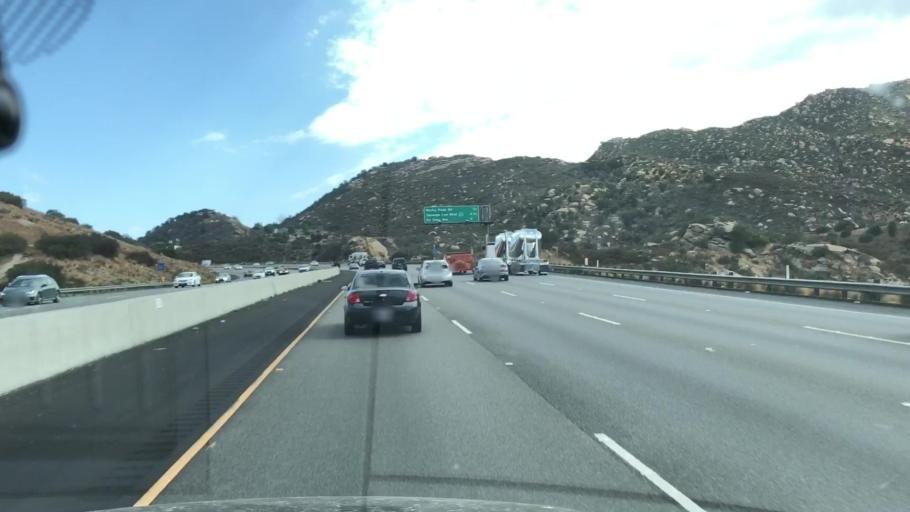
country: US
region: California
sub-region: Los Angeles County
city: Chatsworth
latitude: 34.2684
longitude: -118.6453
